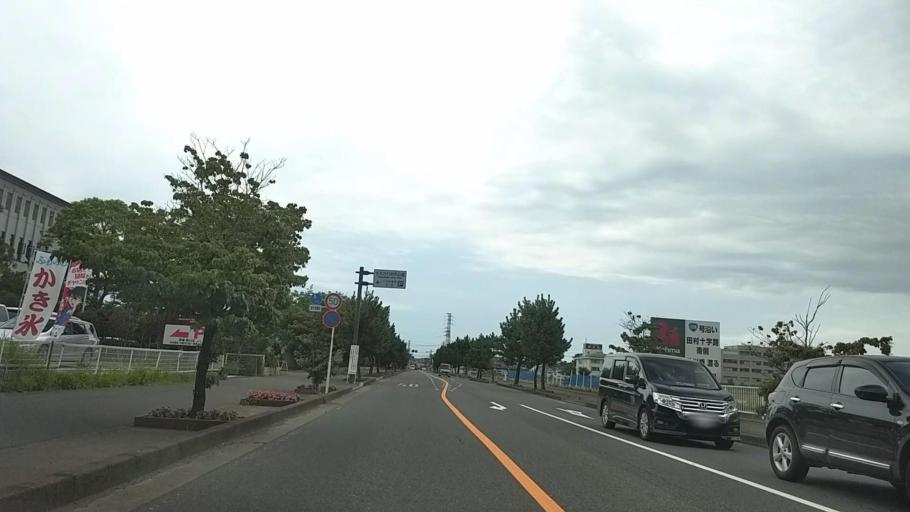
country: JP
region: Kanagawa
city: Chigasaki
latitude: 35.3763
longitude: 139.3844
